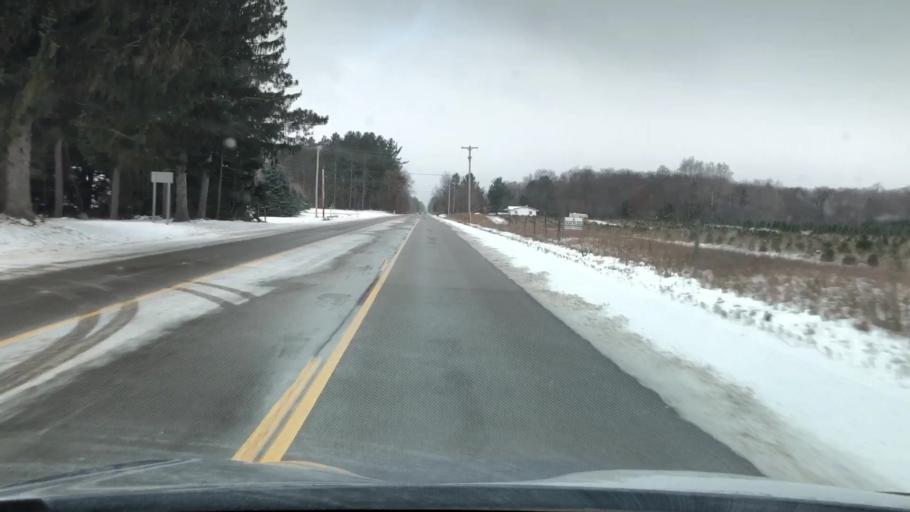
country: US
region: Michigan
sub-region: Wexford County
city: Cadillac
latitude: 44.2812
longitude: -85.4597
